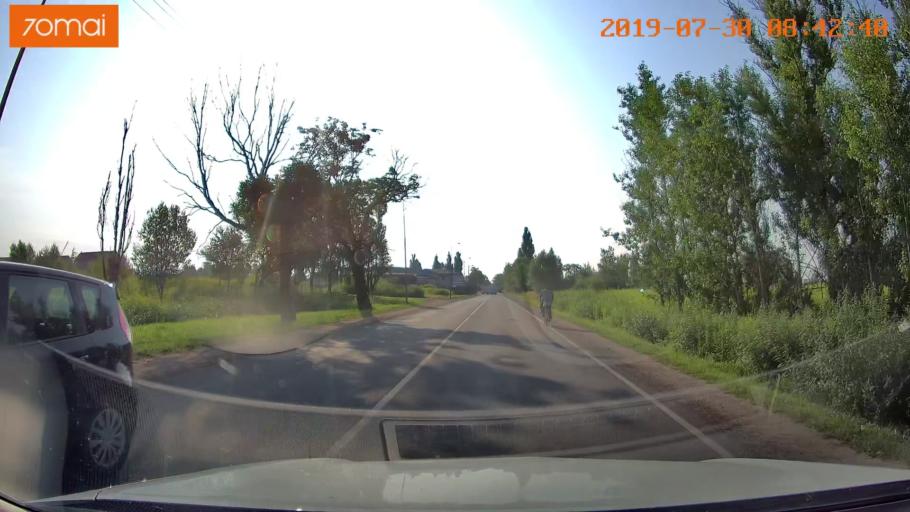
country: RU
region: Kaliningrad
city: Chernyakhovsk
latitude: 54.6291
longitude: 21.8308
